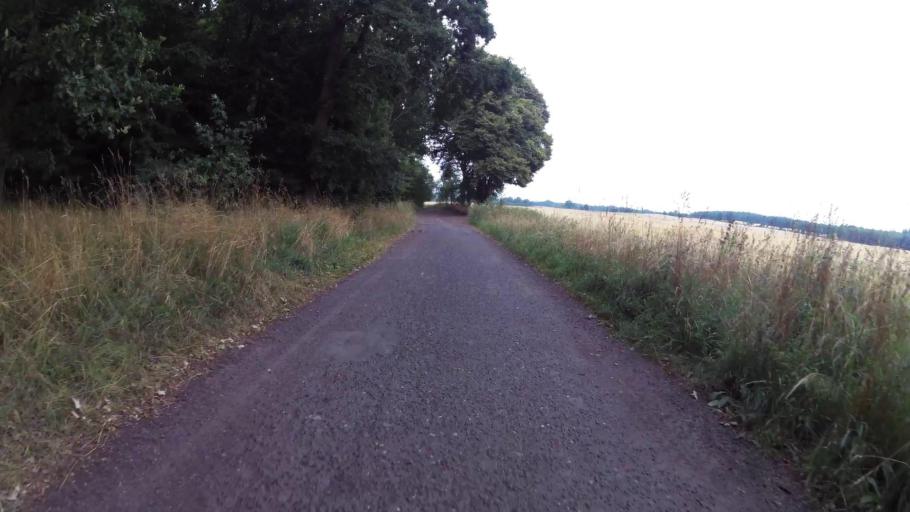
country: PL
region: West Pomeranian Voivodeship
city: Trzcinsko Zdroj
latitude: 52.9003
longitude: 14.6807
